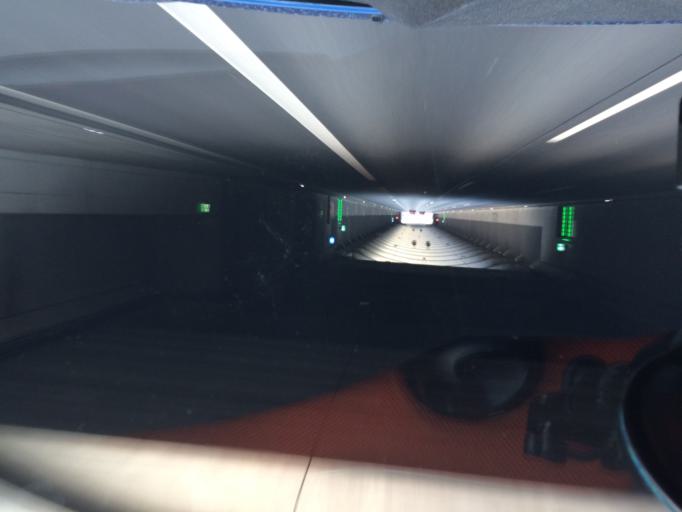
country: DE
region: North Rhine-Westphalia
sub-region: Regierungsbezirk Koln
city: Mengenich
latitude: 50.9419
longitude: 6.8496
